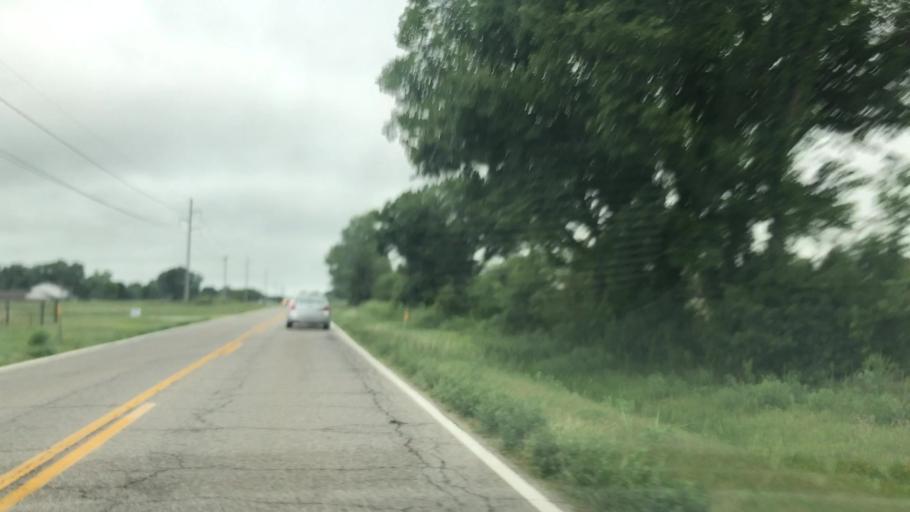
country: US
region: Oklahoma
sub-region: Washington County
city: Dewey
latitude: 36.7280
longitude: -95.8332
